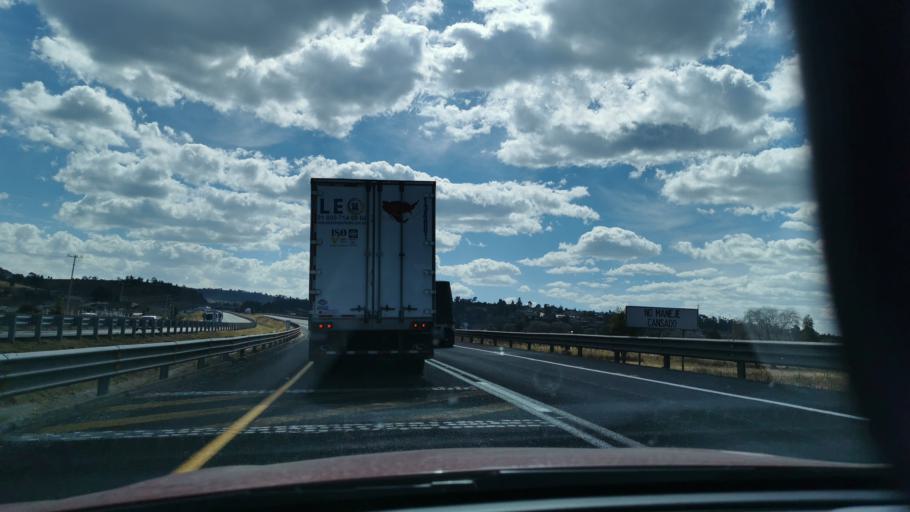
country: MX
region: Mexico
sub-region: Acambay de Ruiz Castaneda
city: La Caridad
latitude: 19.9081
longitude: -99.8534
